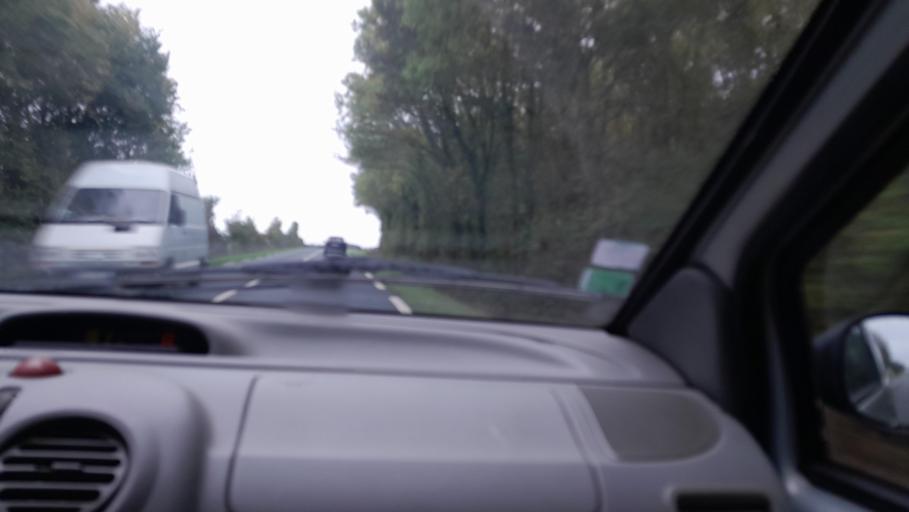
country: FR
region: Pays de la Loire
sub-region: Departement de la Loire-Atlantique
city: Saint-Mars-la-Jaille
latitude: 47.4806
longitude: -1.1739
